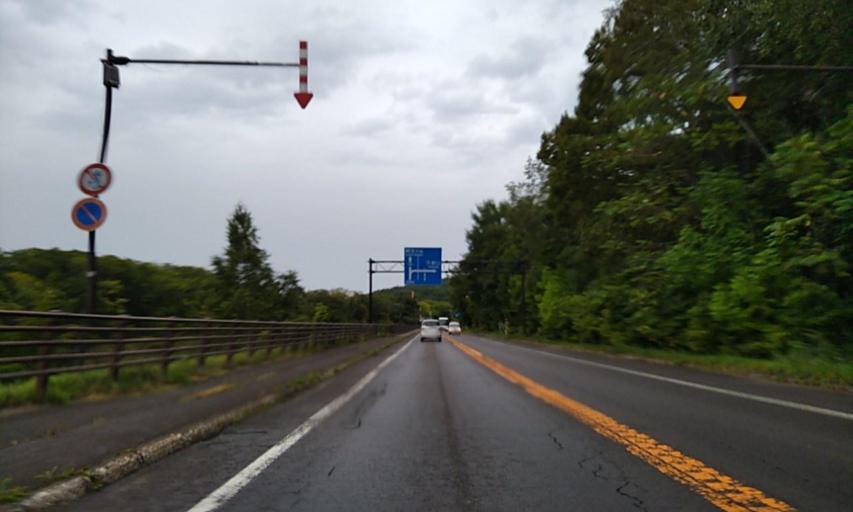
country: JP
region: Hokkaido
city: Abashiri
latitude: 44.0017
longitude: 144.2247
